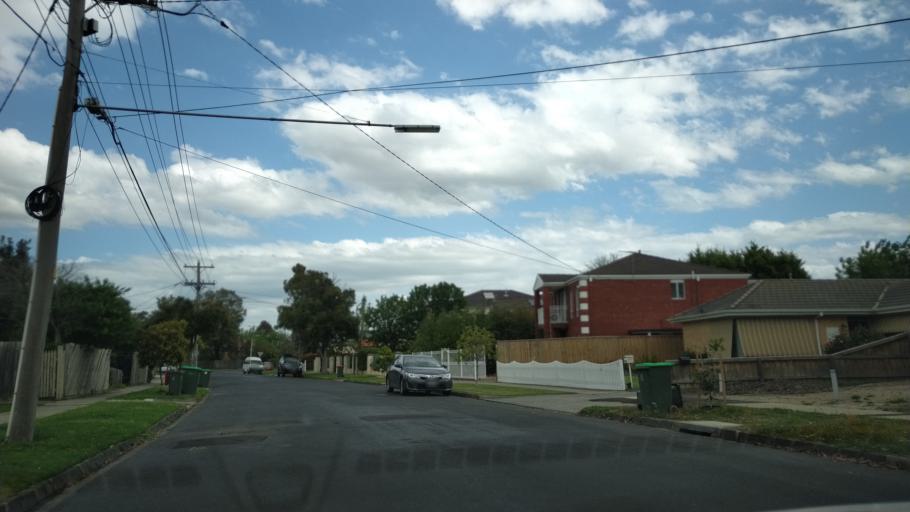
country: AU
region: Victoria
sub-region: Glen Eira
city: Carnegie
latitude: -37.8916
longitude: 145.0527
